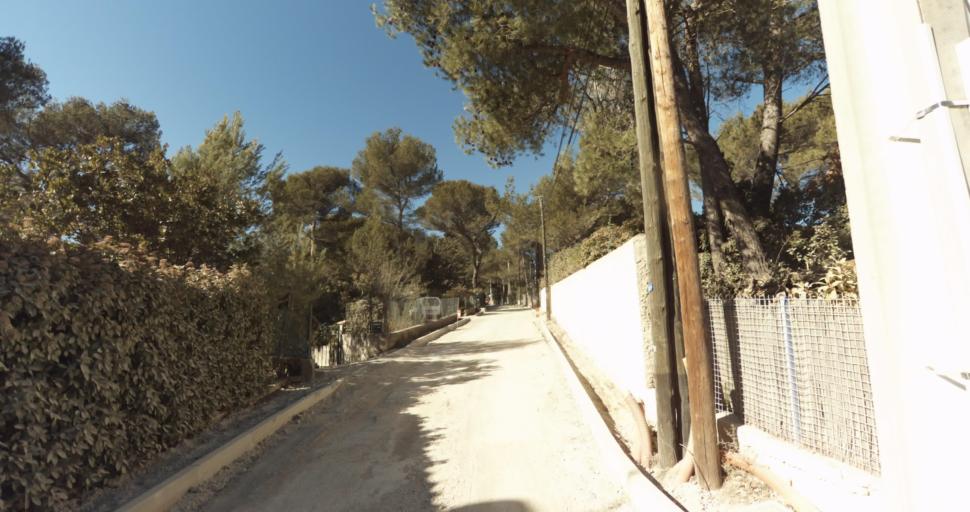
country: FR
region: Provence-Alpes-Cote d'Azur
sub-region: Departement des Bouches-du-Rhone
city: Peypin
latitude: 43.3866
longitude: 5.5730
